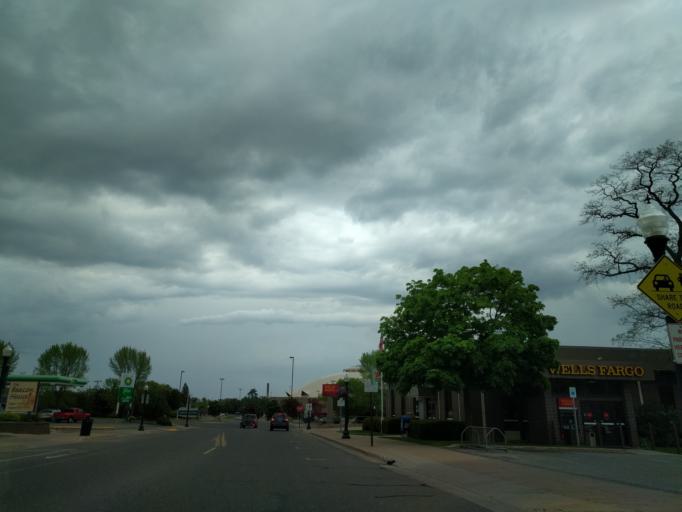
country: US
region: Michigan
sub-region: Marquette County
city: Marquette
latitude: 46.5557
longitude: -87.3948
